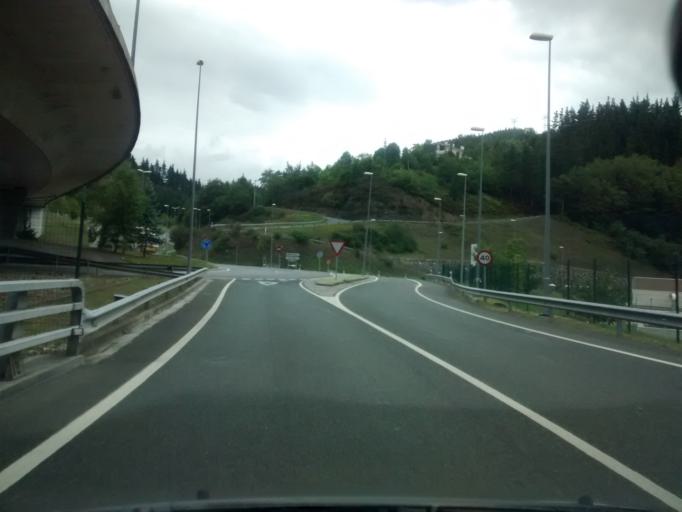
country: ES
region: Basque Country
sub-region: Provincia de Guipuzcoa
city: Arrasate / Mondragon
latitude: 43.0755
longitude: -2.4621
